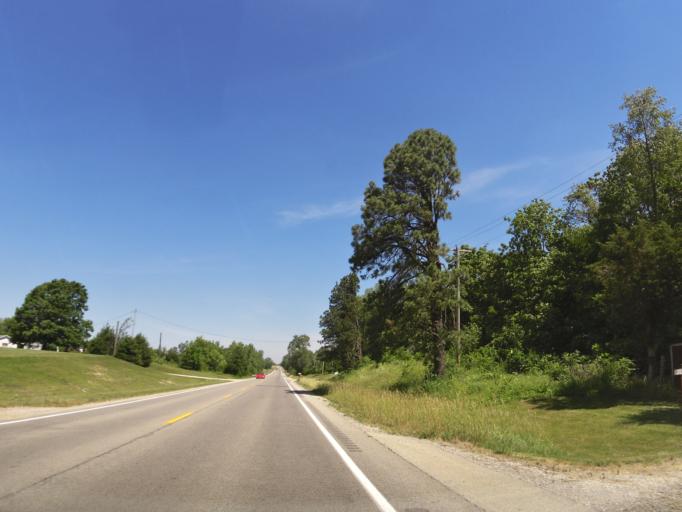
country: US
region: Illinois
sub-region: Vermilion County
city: Danville
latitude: 40.2372
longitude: -87.6438
